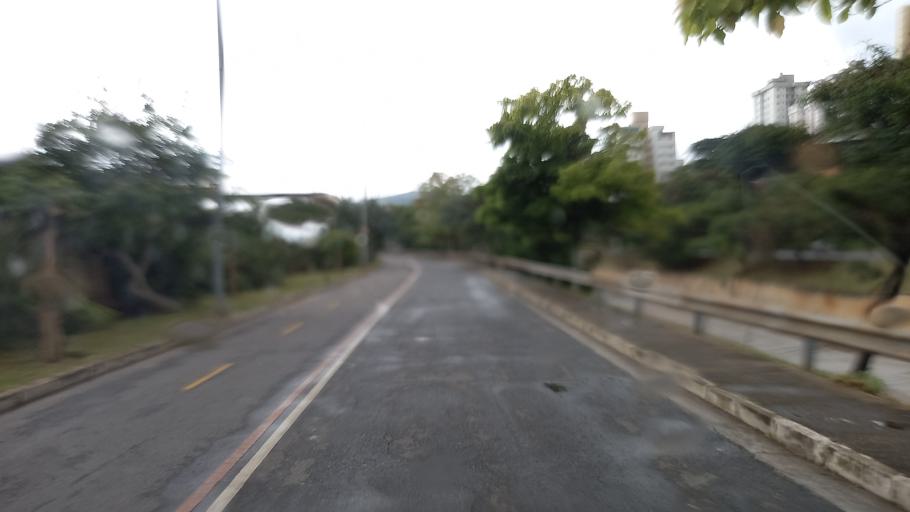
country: BR
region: Minas Gerais
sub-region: Belo Horizonte
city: Belo Horizonte
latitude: -19.9193
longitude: -43.9171
